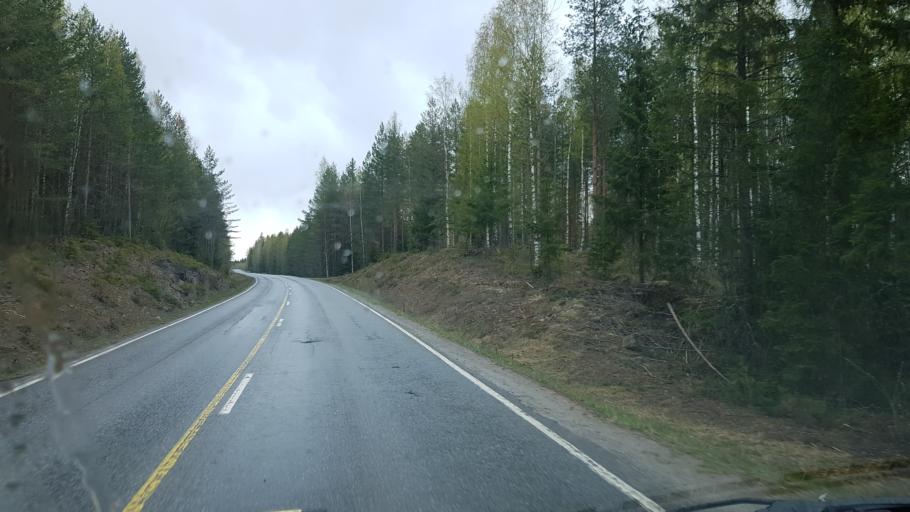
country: FI
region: Pirkanmaa
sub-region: Tampere
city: Pirkkala
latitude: 61.3971
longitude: 23.6275
